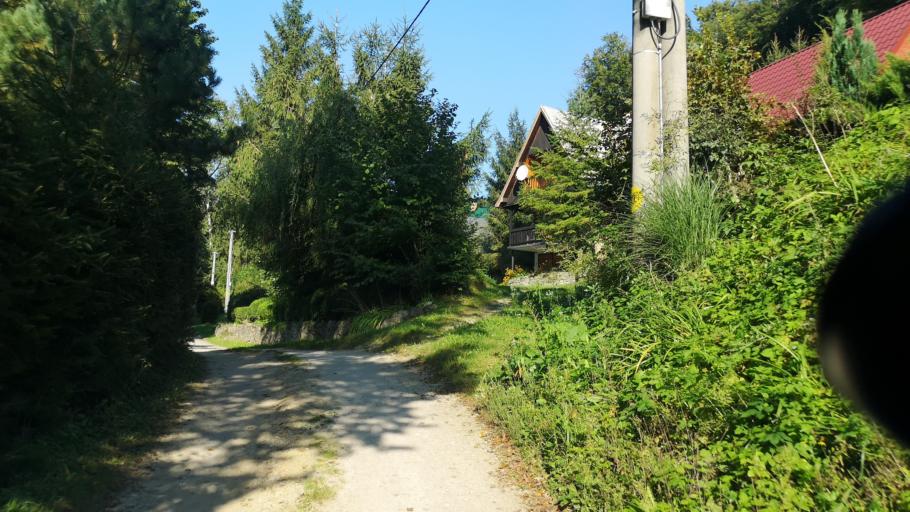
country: SK
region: Trnavsky
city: Smolenice
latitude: 48.5659
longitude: 17.4231
